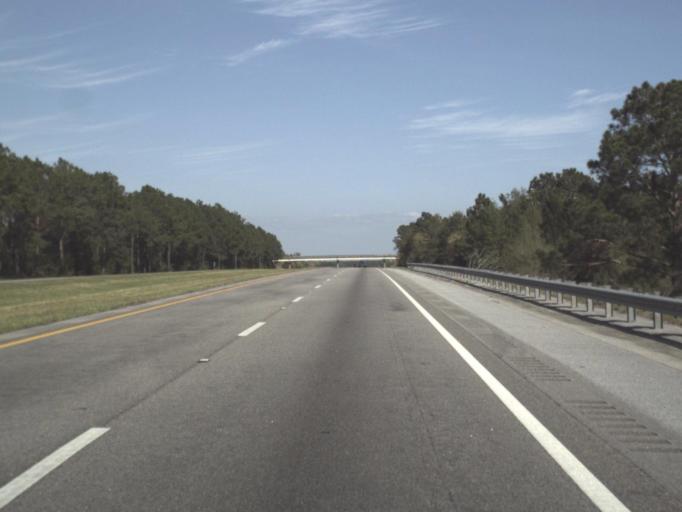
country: US
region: Florida
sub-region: Okaloosa County
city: Crestview
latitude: 30.7188
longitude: -86.4600
